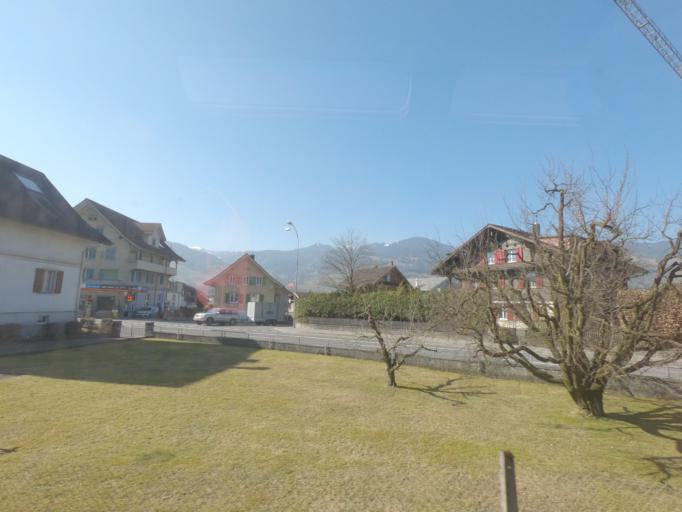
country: CH
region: Obwalden
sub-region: Obwalden
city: Giswil
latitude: 46.8382
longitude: 8.1878
